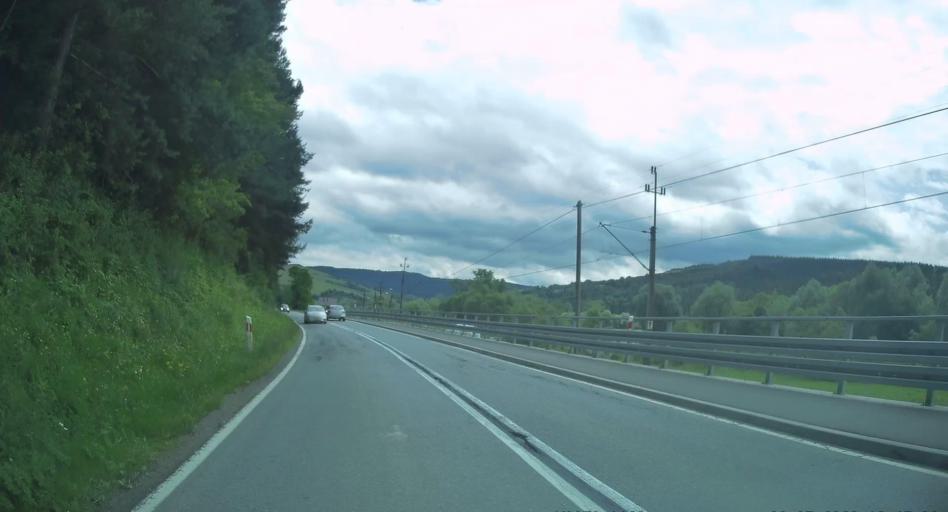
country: PL
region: Lesser Poland Voivodeship
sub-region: Powiat nowosadecki
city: Muszyna
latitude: 49.3440
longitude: 20.8189
